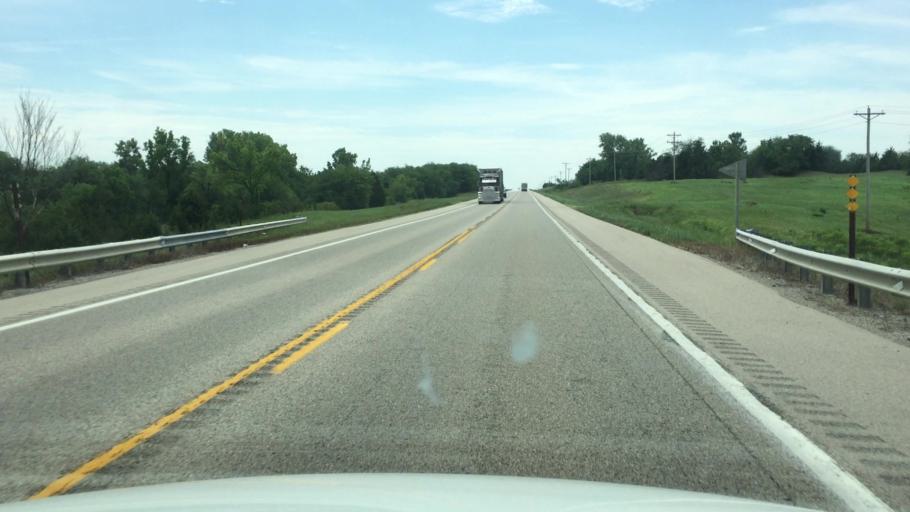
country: US
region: Kansas
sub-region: Nemaha County
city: Sabetha
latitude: 39.7224
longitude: -95.7299
